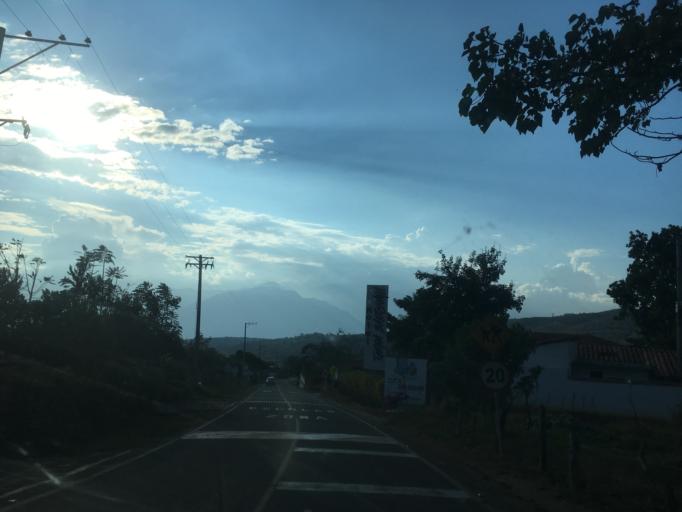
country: CO
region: Santander
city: Barichara
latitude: 6.6411
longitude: -73.1907
